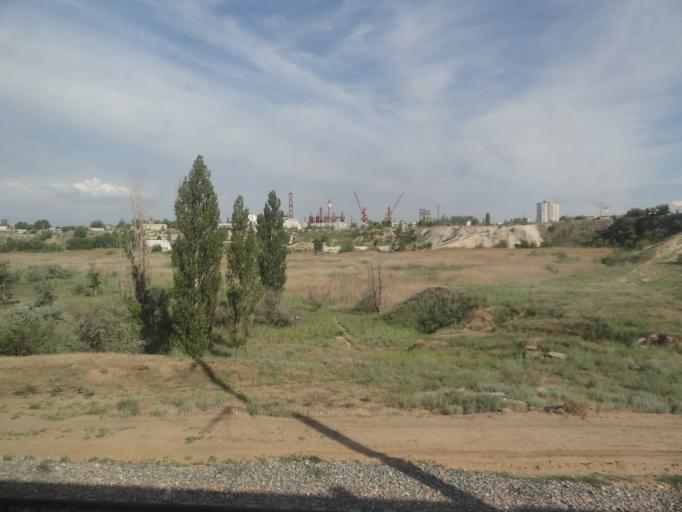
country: RU
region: Volgograd
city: Gorodishche
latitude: 48.7784
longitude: 44.4667
